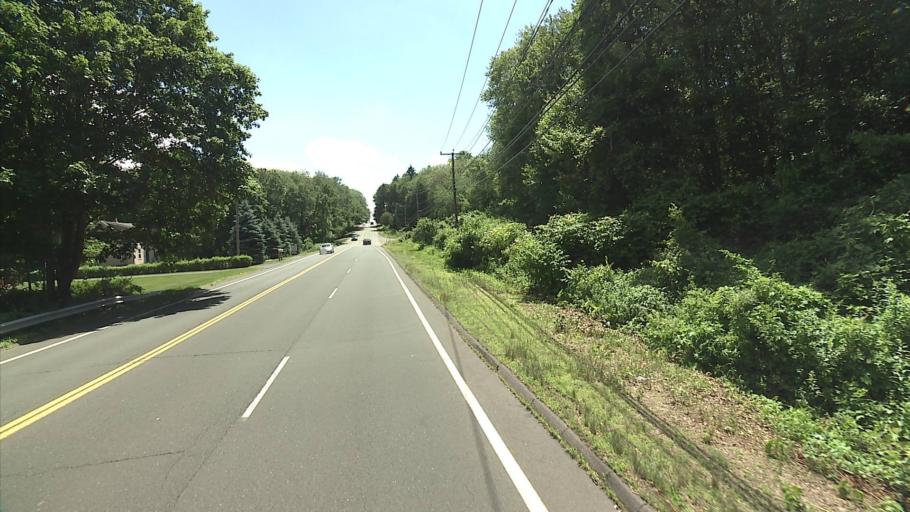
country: US
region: Connecticut
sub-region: New Haven County
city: Prospect
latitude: 41.4480
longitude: -72.9885
